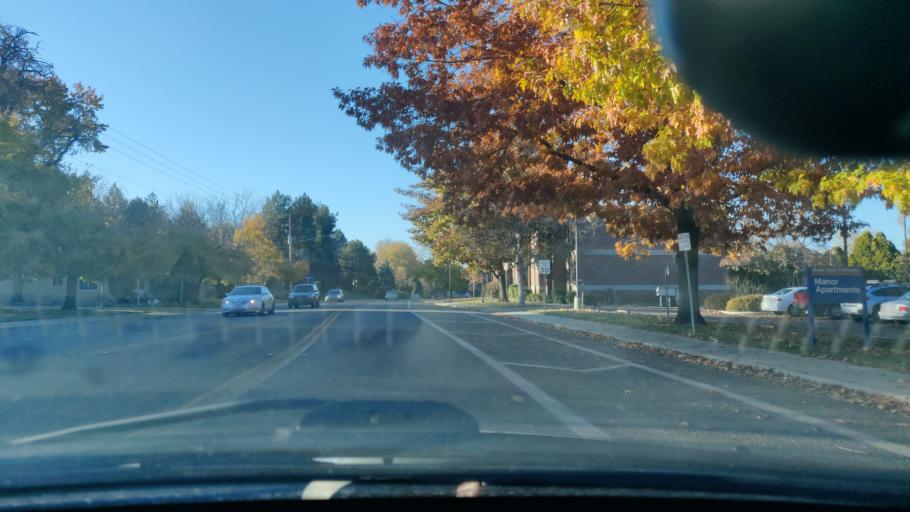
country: US
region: Idaho
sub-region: Ada County
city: Boise
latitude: 43.5984
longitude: -116.2053
